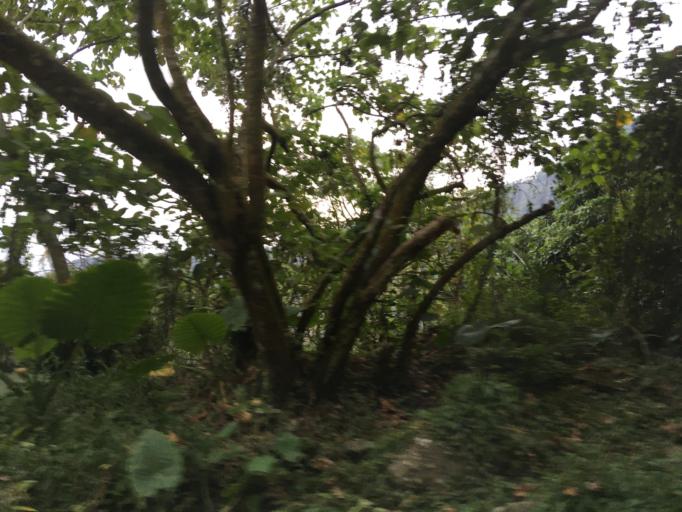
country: TW
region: Taiwan
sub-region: Chiayi
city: Jiayi Shi
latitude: 23.5366
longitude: 120.6067
